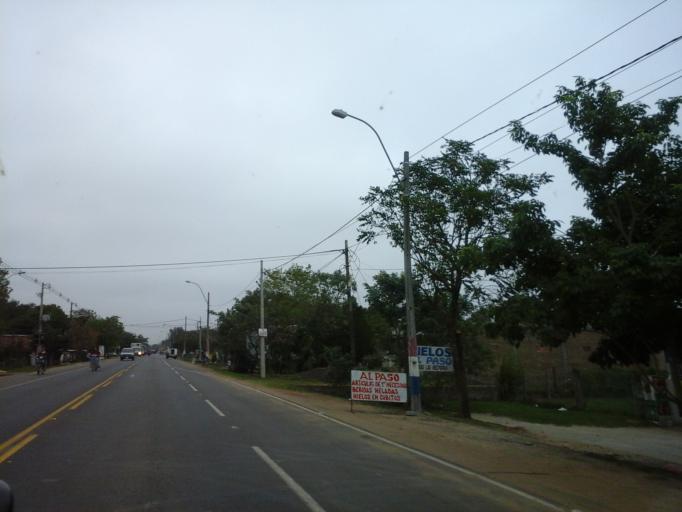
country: PY
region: Neembucu
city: Pilar
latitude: -26.8412
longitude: -58.2908
